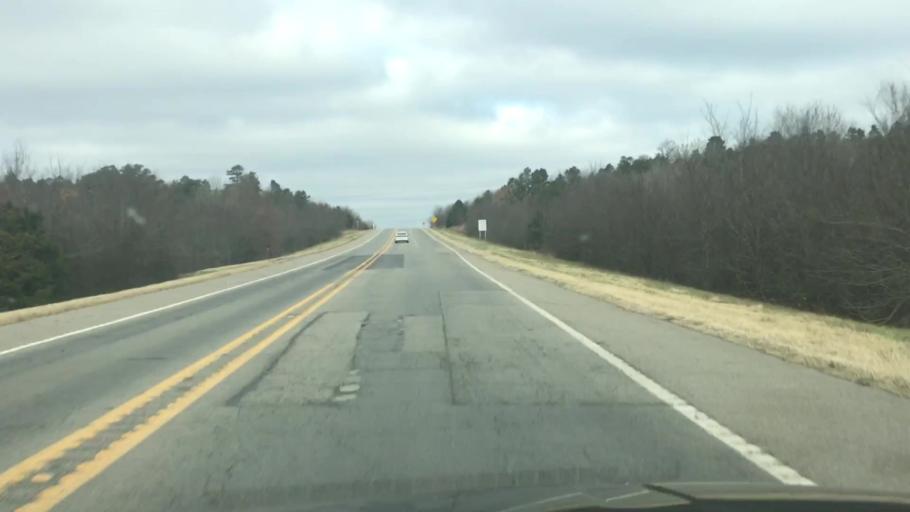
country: US
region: Arkansas
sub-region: Scott County
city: Waldron
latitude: 34.8594
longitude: -94.0697
